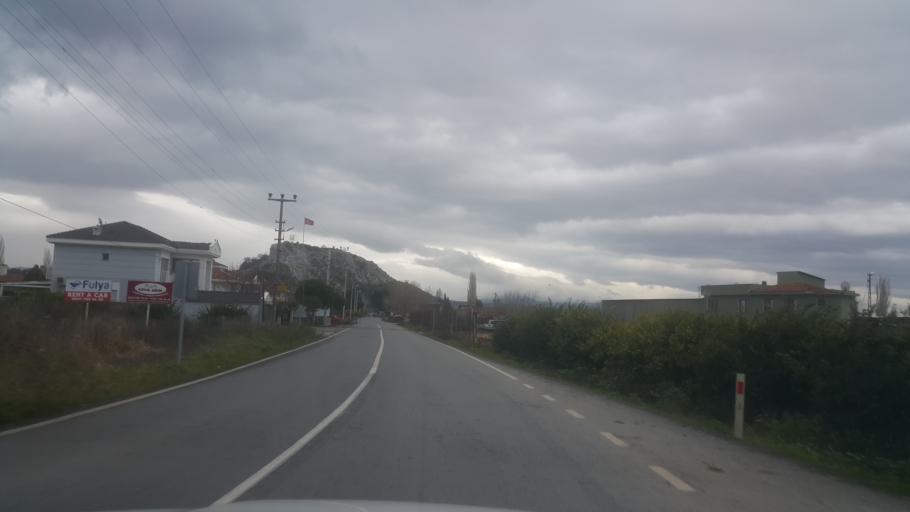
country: TR
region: Izmir
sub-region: Seferihisar
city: Seferhisar
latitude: 38.1910
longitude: 26.7998
